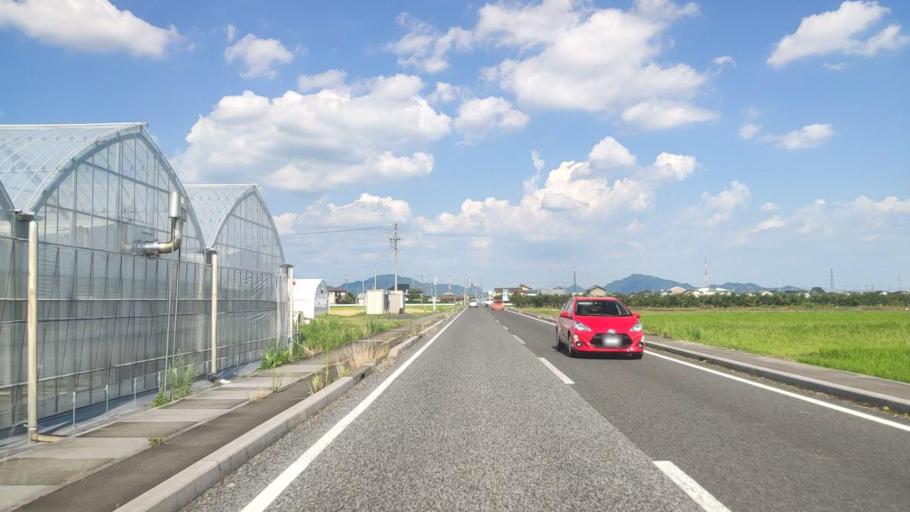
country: JP
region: Gifu
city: Gifu-shi
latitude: 35.4501
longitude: 136.6875
